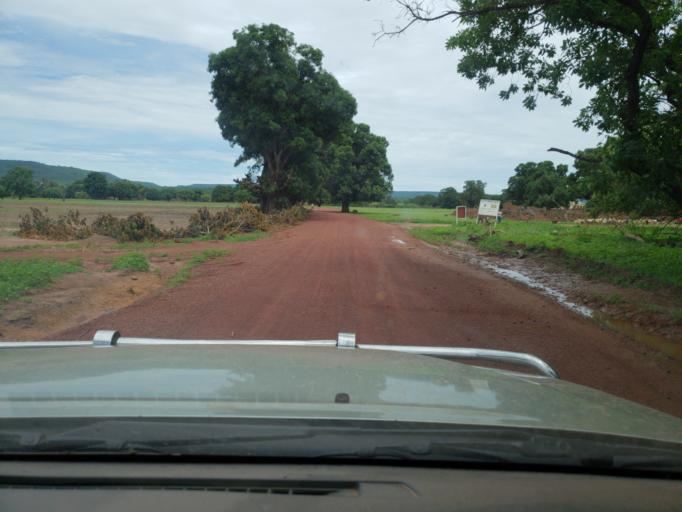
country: ML
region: Sikasso
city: Sikasso
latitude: 11.6723
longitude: -6.3387
